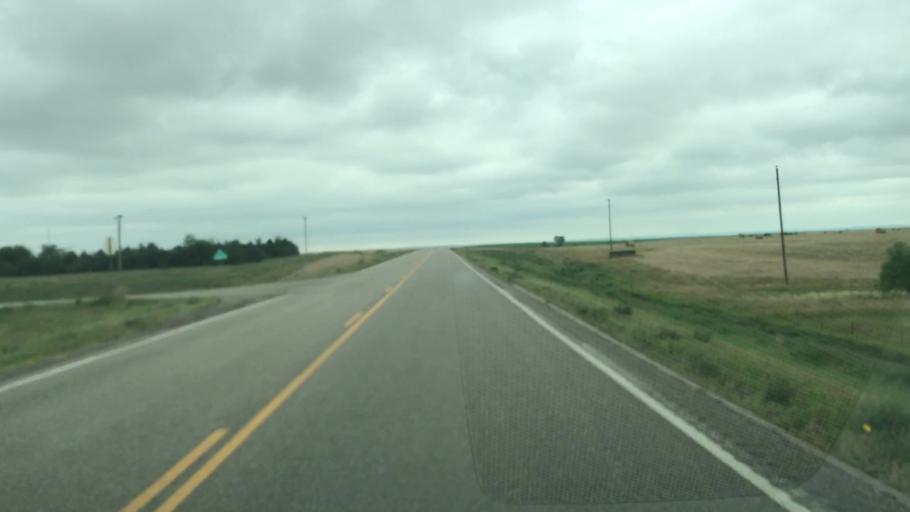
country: US
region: South Dakota
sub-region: Jackson County
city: Kadoka
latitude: 43.8217
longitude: -101.5224
